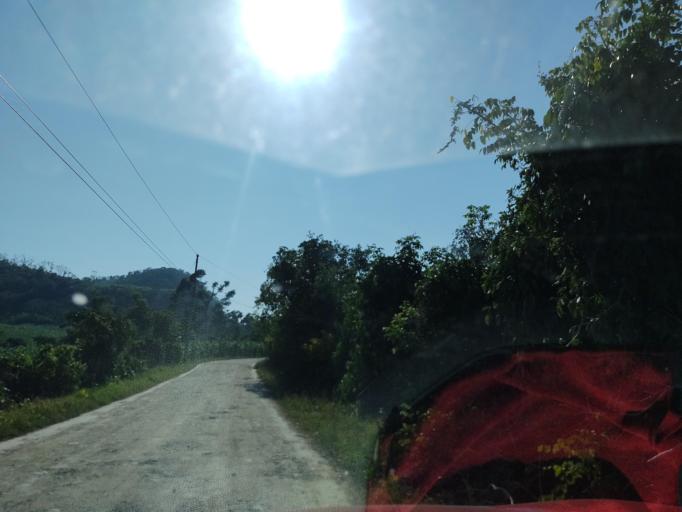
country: MX
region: Veracruz
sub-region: Papantla
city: Polutla
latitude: 20.4929
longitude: -97.1804
